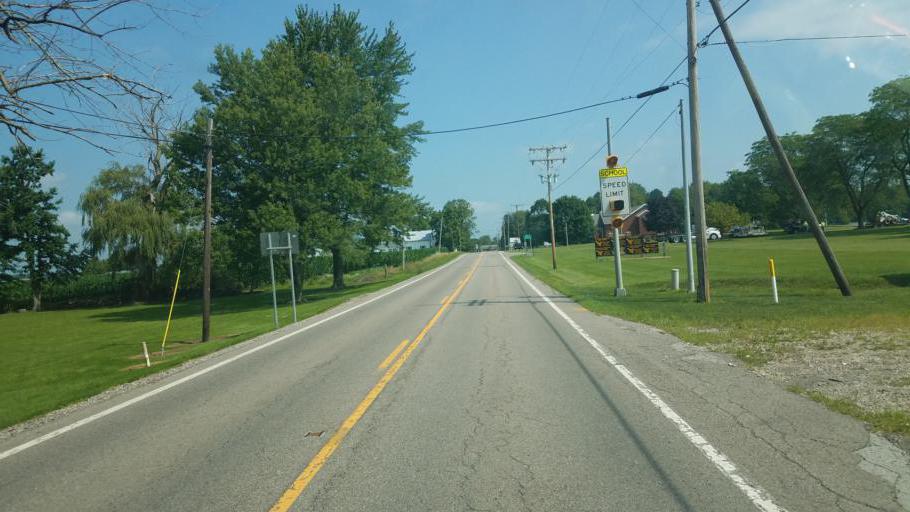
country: US
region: Ohio
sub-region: Crawford County
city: Galion
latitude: 40.7872
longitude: -82.8572
